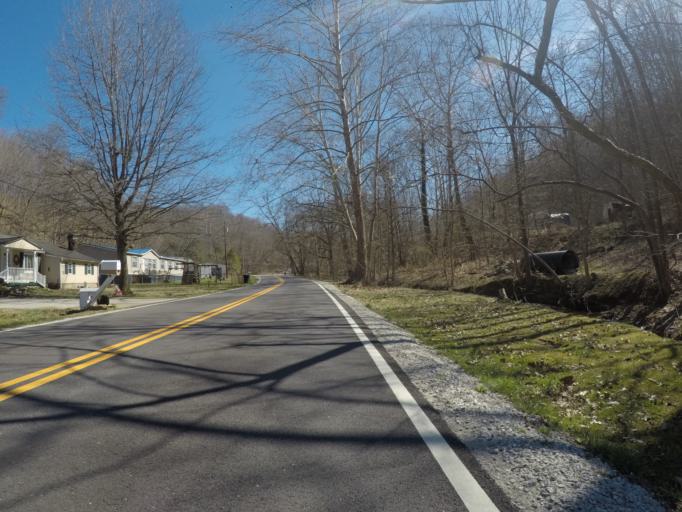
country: US
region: Ohio
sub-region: Lawrence County
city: South Point
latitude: 38.4643
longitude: -82.5628
